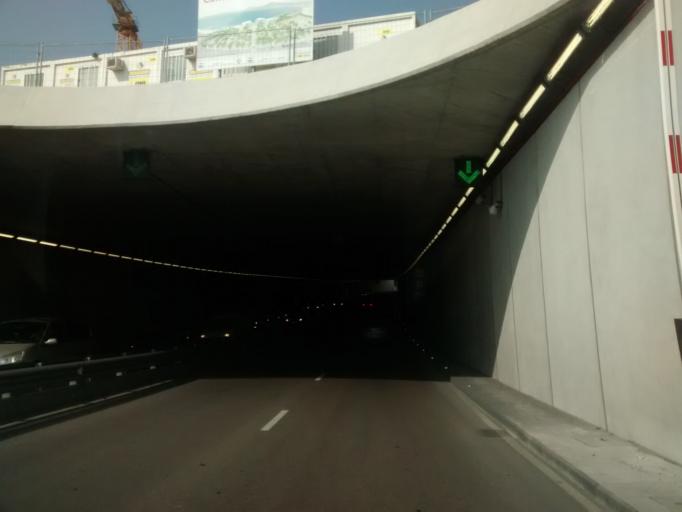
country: ES
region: Cantabria
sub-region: Provincia de Cantabria
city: Santander
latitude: 43.4613
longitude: -3.8031
